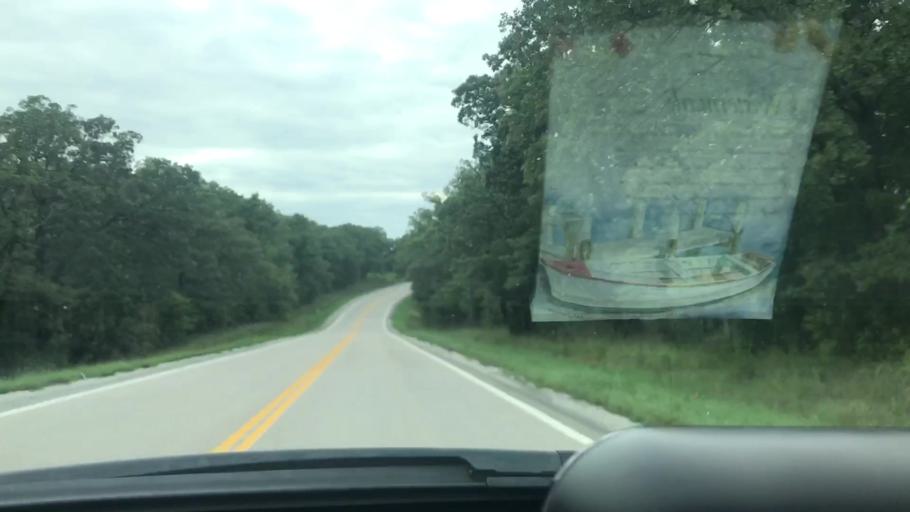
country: US
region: Missouri
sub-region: Benton County
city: Warsaw
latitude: 38.1622
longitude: -93.3015
